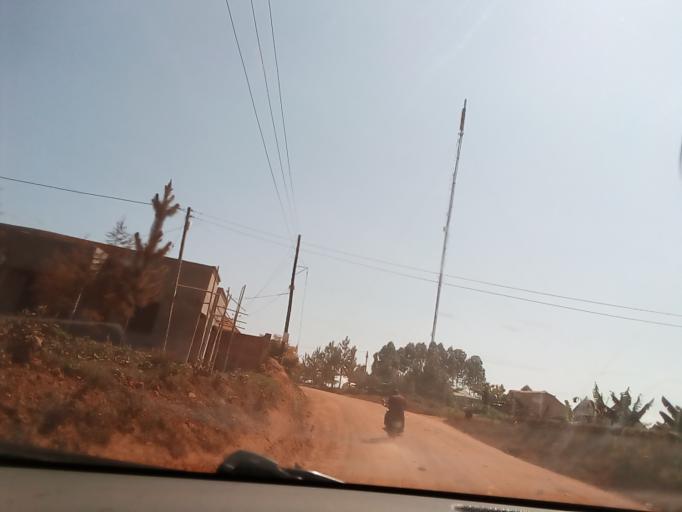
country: UG
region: Central Region
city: Masaka
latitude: -0.3650
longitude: 31.7489
